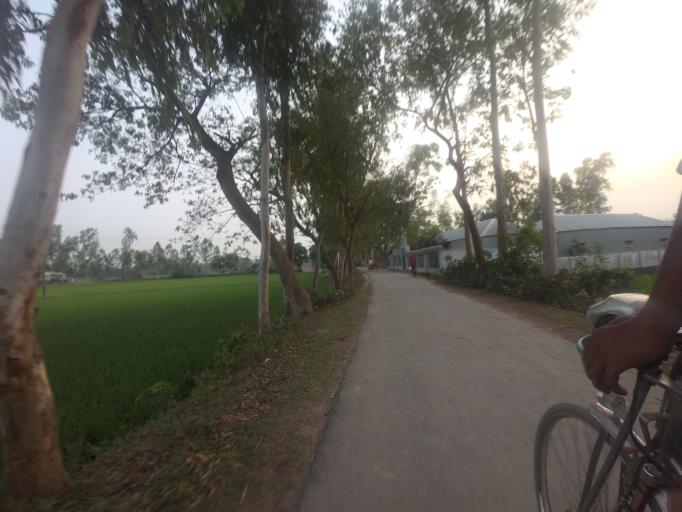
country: BD
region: Rajshahi
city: Sirajganj
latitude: 24.3235
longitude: 89.6749
